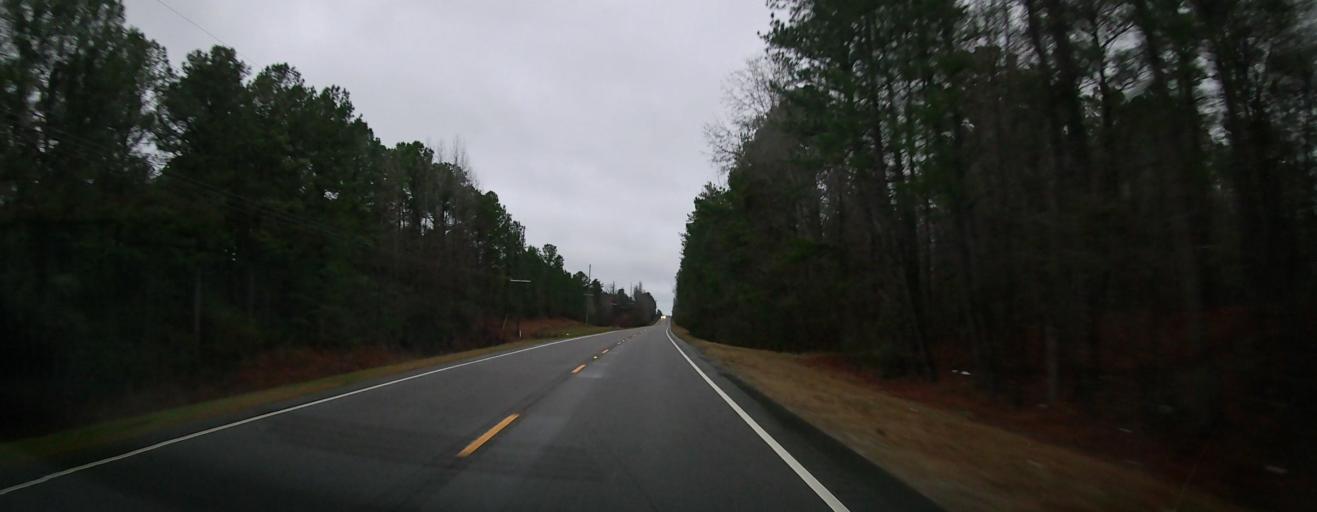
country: US
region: Alabama
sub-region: Bibb County
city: West Blocton
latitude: 33.0929
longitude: -87.1379
